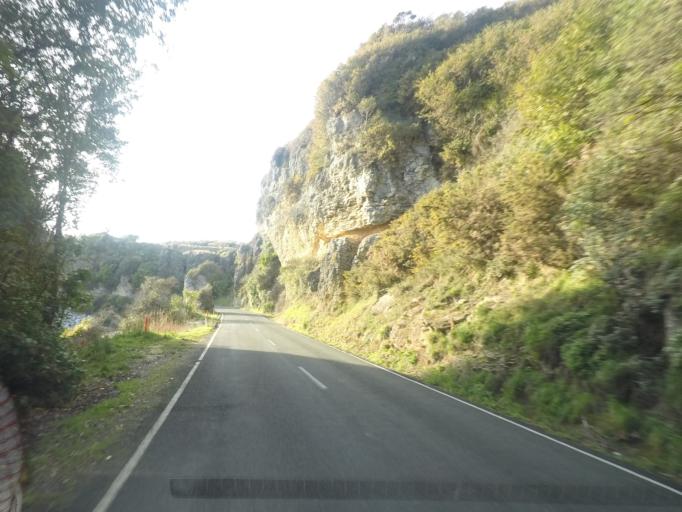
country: NZ
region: Tasman
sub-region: Tasman District
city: Takaka
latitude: -40.8223
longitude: 172.8995
